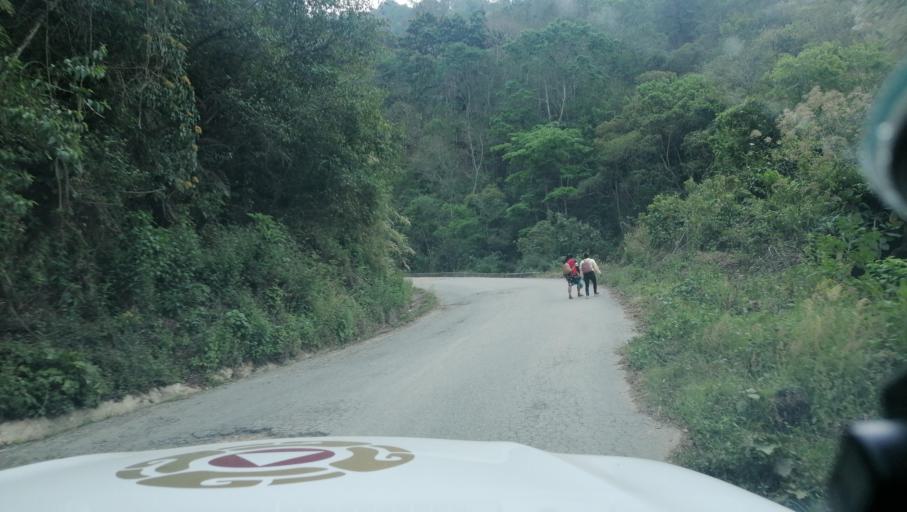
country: GT
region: San Marcos
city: Tacana
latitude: 15.2122
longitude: -92.1991
